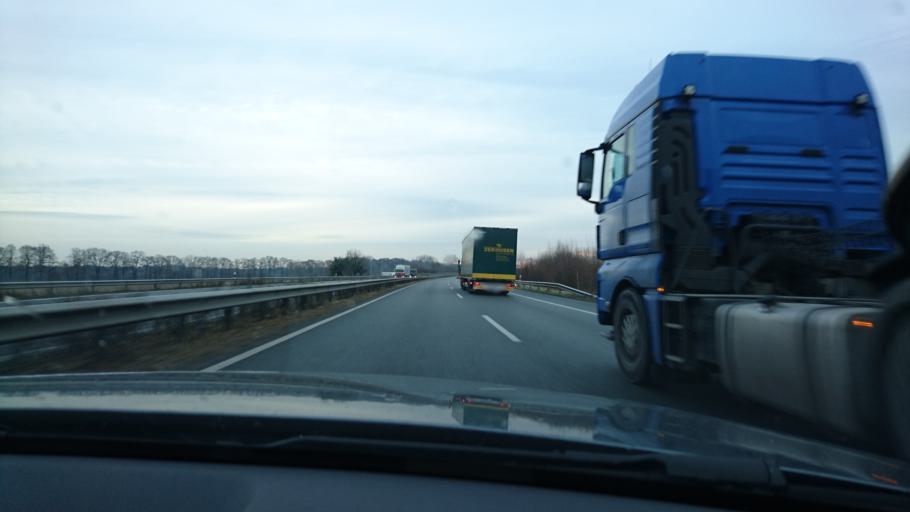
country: DE
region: Lower Saxony
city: Salzbergen
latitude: 52.3404
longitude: 7.4033
